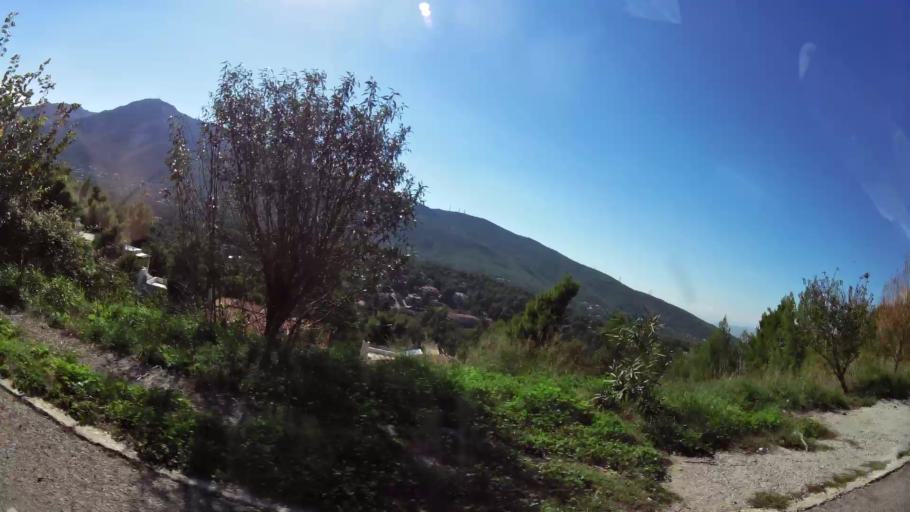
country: GR
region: Attica
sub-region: Nomarchia Anatolikis Attikis
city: Rodopoli
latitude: 38.1101
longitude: 23.8857
